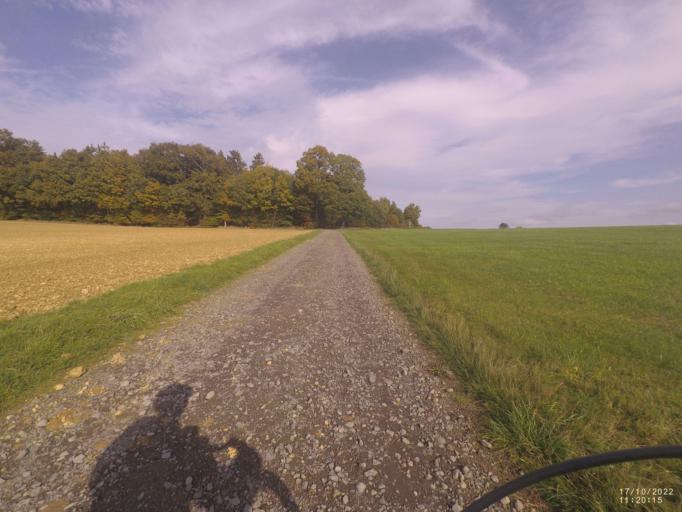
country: DE
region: Rheinland-Pfalz
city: Steiningen
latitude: 50.1941
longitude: 6.9231
